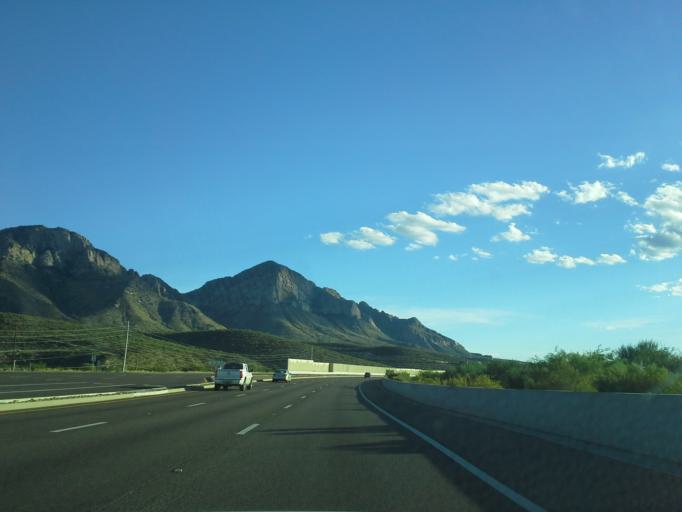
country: US
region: Arizona
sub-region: Pima County
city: Oro Valley
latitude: 32.4165
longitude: -110.9378
